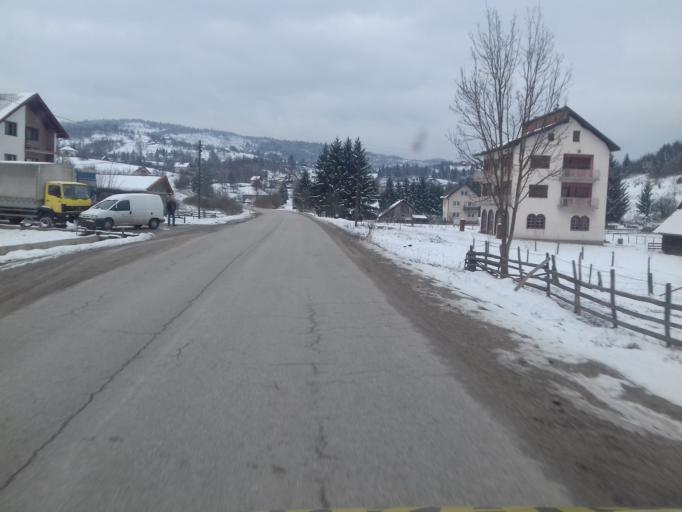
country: BA
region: Republika Srpska
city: Pale
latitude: 43.8683
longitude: 18.5541
